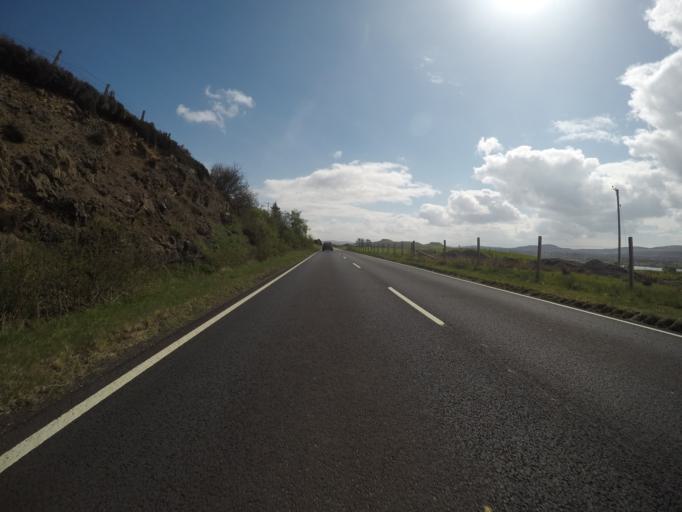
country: GB
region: Scotland
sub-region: Highland
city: Portree
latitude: 57.4960
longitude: -6.3217
